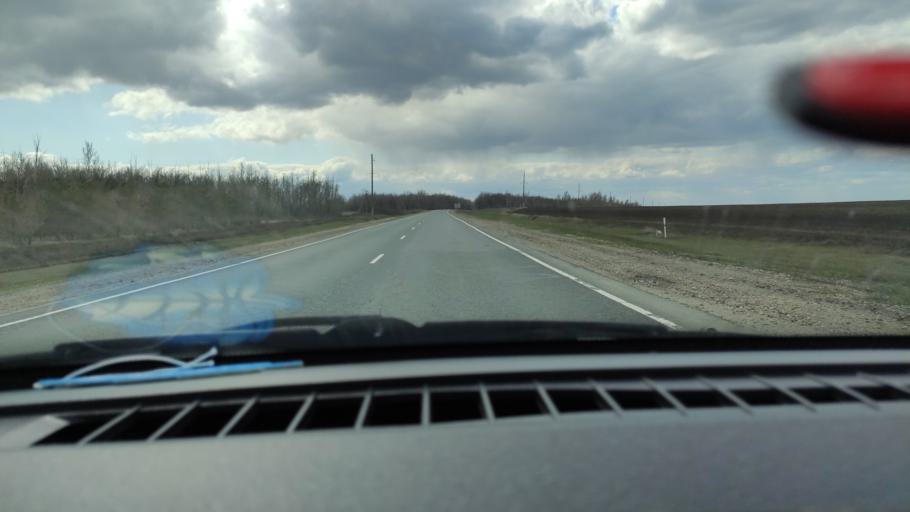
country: RU
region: Saratov
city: Alekseyevka
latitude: 52.2717
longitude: 47.9293
